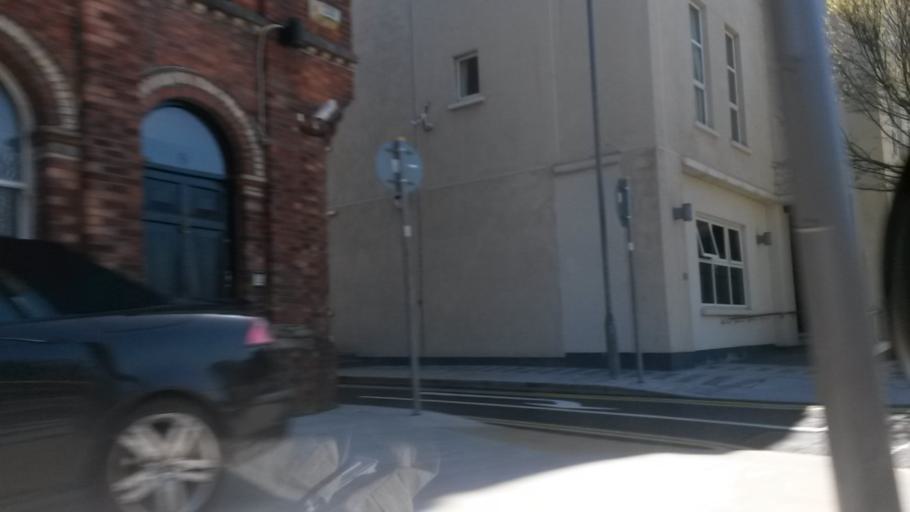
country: IE
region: Munster
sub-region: County Cork
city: Cork
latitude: 51.8996
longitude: -8.4832
